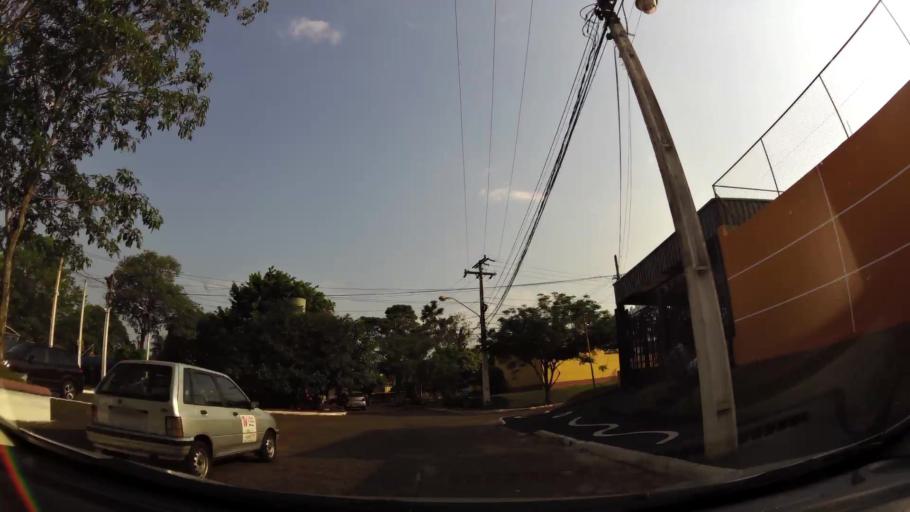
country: PY
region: Alto Parana
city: Presidente Franco
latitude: -25.5265
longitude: -54.6321
